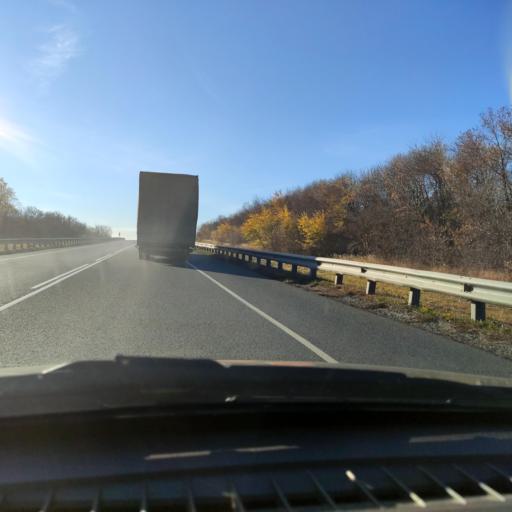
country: RU
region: Samara
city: Obsharovka
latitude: 53.2300
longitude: 48.9105
